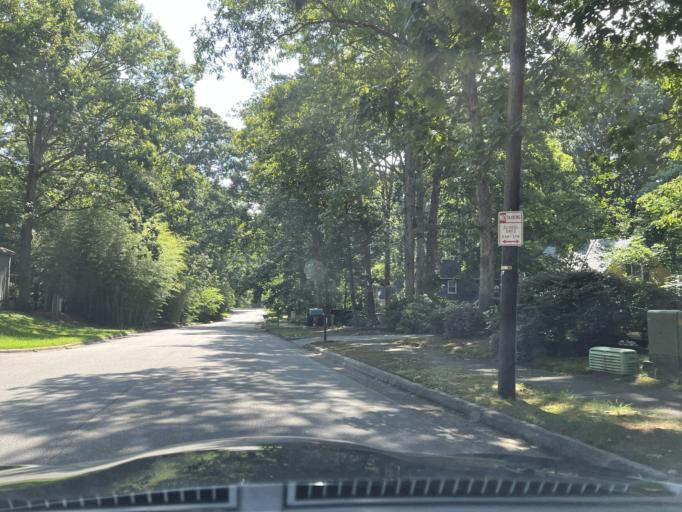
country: US
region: North Carolina
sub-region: Wake County
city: West Raleigh
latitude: 35.8684
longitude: -78.6018
